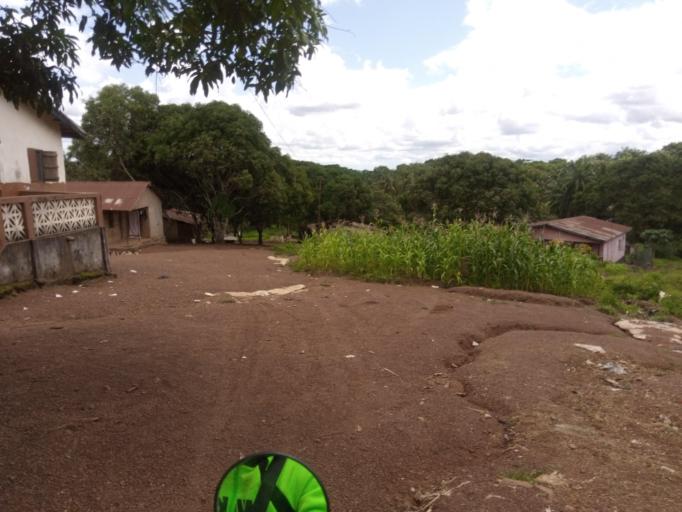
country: SL
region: Northern Province
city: Port Loko
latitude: 8.7618
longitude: -12.7831
